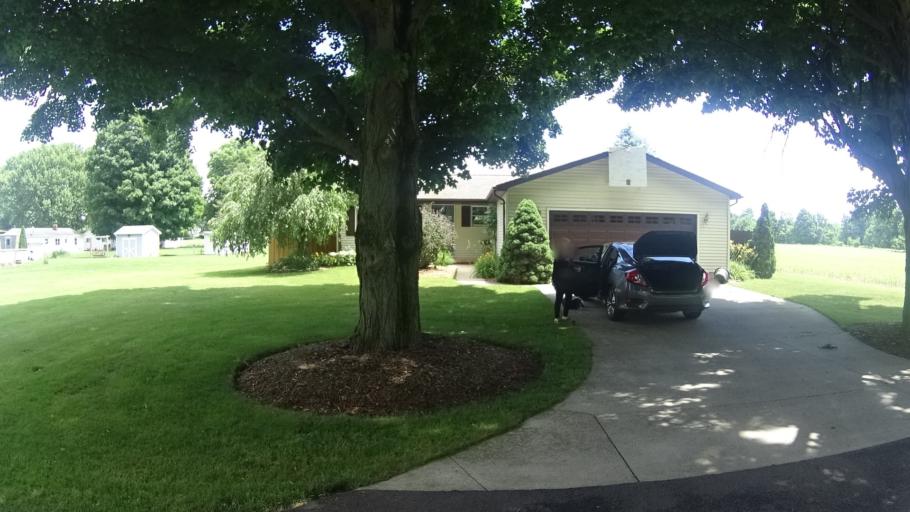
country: US
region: Ohio
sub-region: Erie County
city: Milan
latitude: 41.2935
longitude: -82.6104
